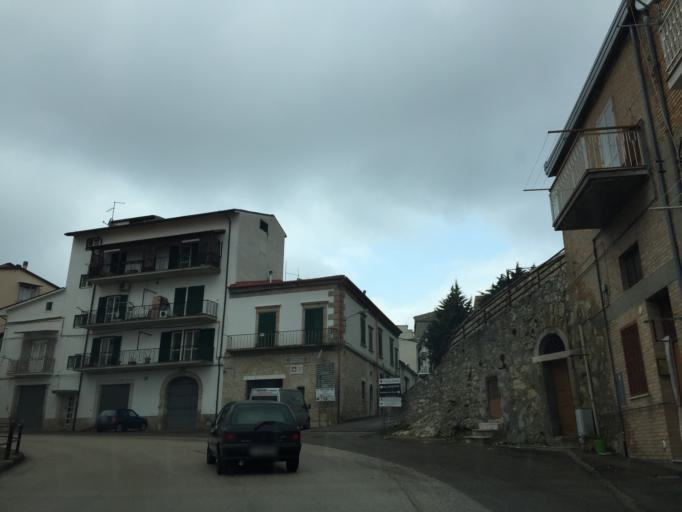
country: IT
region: Apulia
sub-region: Provincia di Foggia
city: Bovino
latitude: 41.2494
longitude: 15.3433
